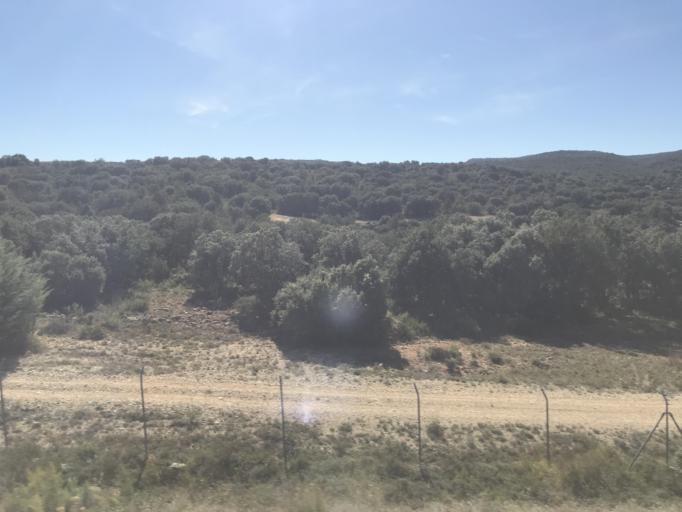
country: ES
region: Castille and Leon
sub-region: Provincia de Soria
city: Arcos de Jalon
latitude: 41.1772
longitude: -2.2328
